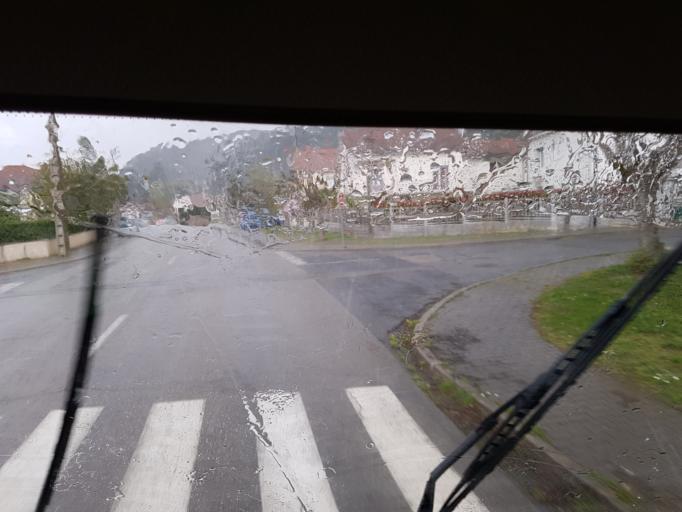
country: FR
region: Auvergne
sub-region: Departement de la Haute-Loire
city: Aurec-sur-Loire
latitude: 45.3642
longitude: 4.2020
